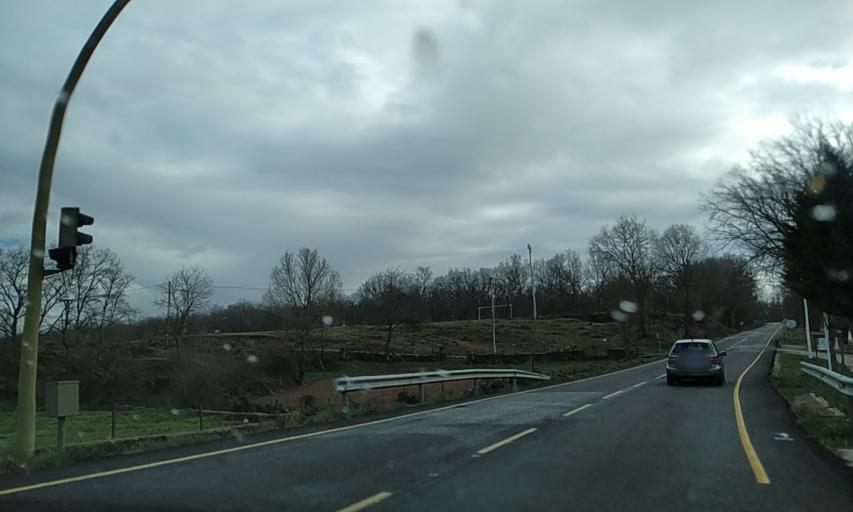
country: ES
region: Castille and Leon
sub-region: Provincia de Salamanca
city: Villasrubias
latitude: 40.3365
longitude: -6.6417
